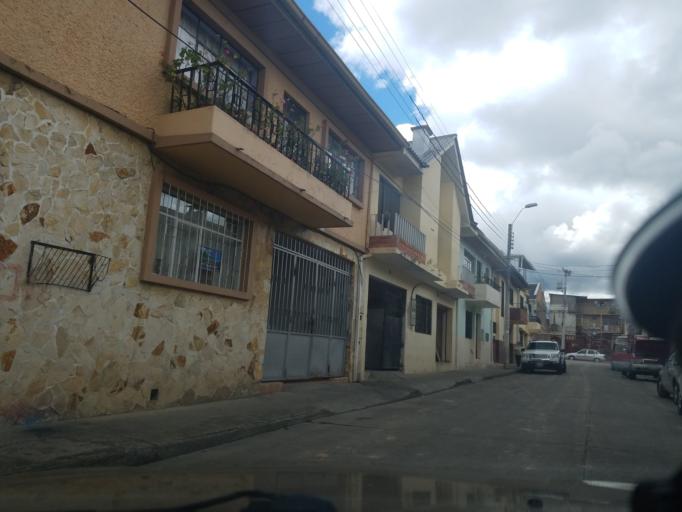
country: EC
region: Azuay
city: Cuenca
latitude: -2.8879
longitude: -78.9953
